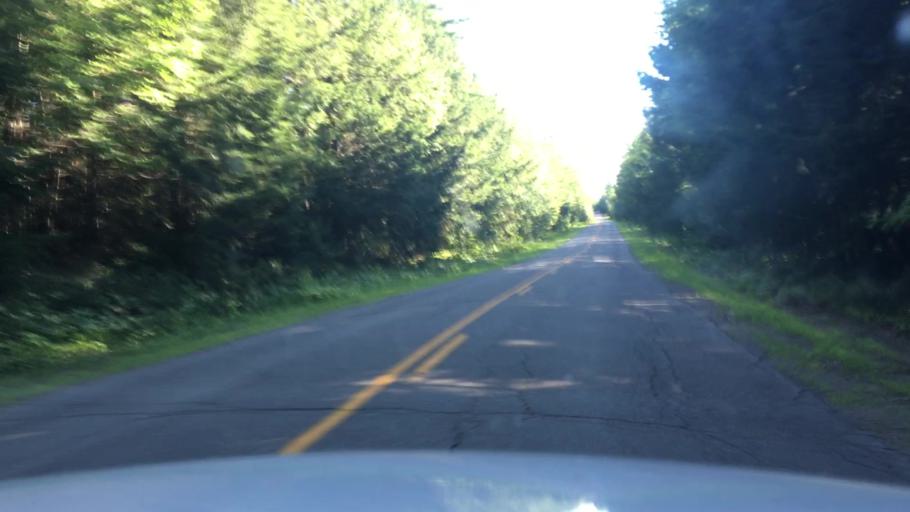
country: US
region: Maine
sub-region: Penobscot County
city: Enfield
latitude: 45.2202
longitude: -68.5812
